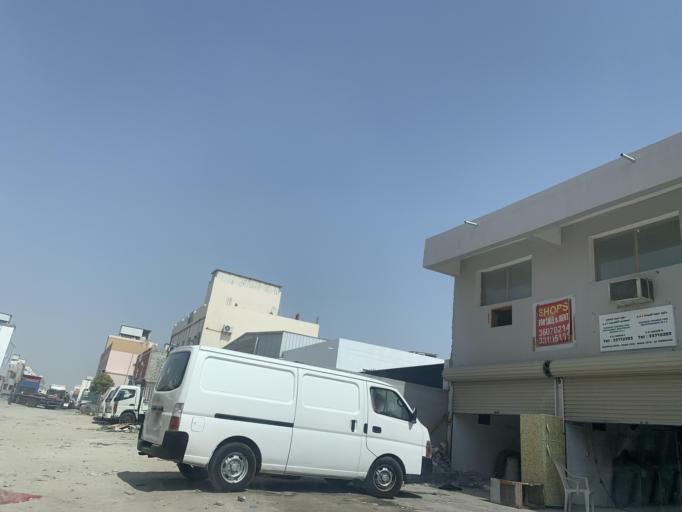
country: BH
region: Central Governorate
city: Madinat Hamad
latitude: 26.1398
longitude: 50.4824
